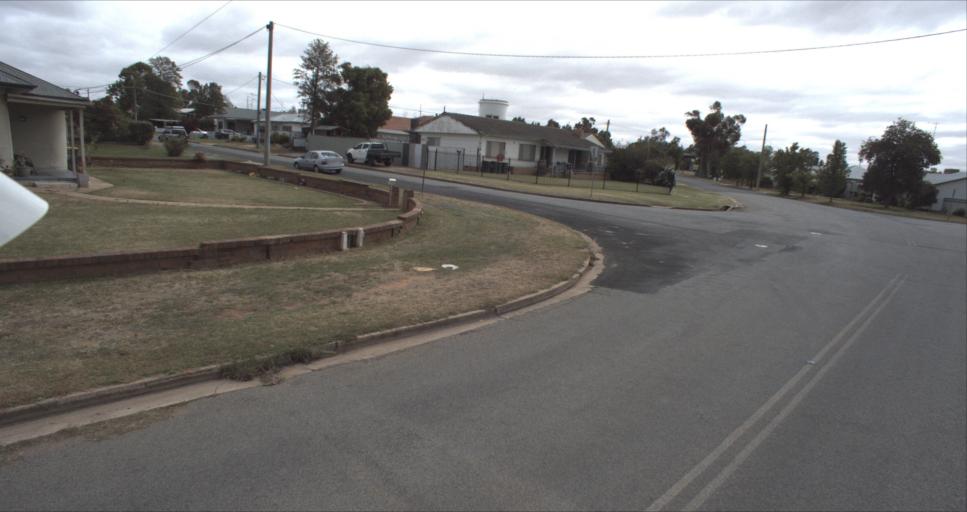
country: AU
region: New South Wales
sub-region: Leeton
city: Leeton
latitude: -34.5646
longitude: 146.3970
